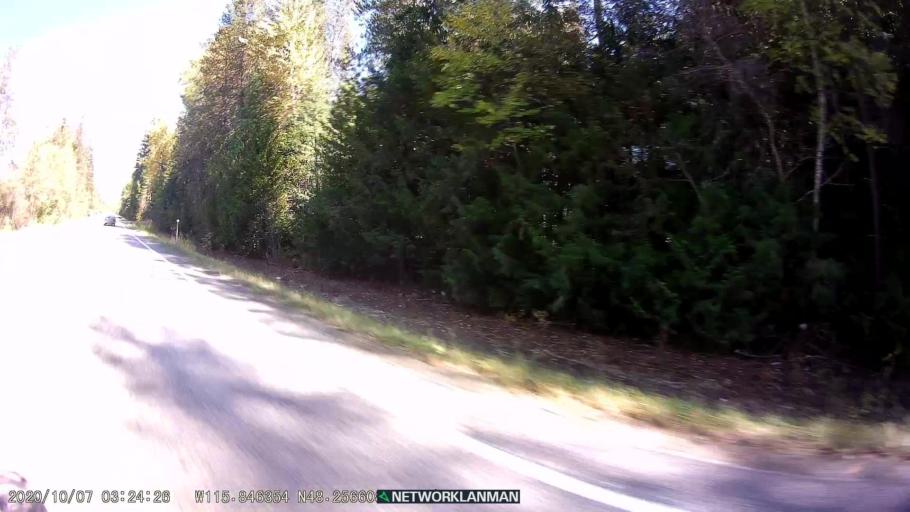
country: US
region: Montana
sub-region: Lincoln County
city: Libby
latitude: 48.2570
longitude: -115.8462
